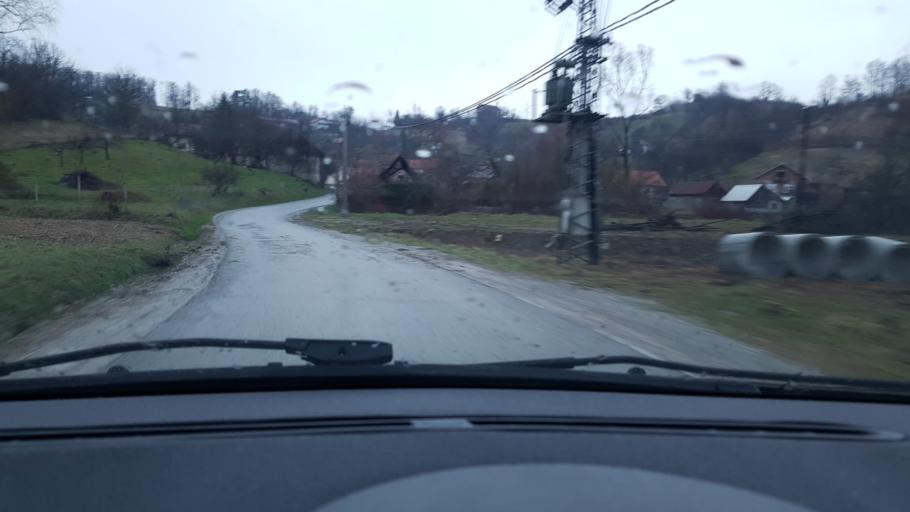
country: HR
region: Krapinsko-Zagorska
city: Bedekovcina
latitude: 45.9897
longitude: 15.9801
